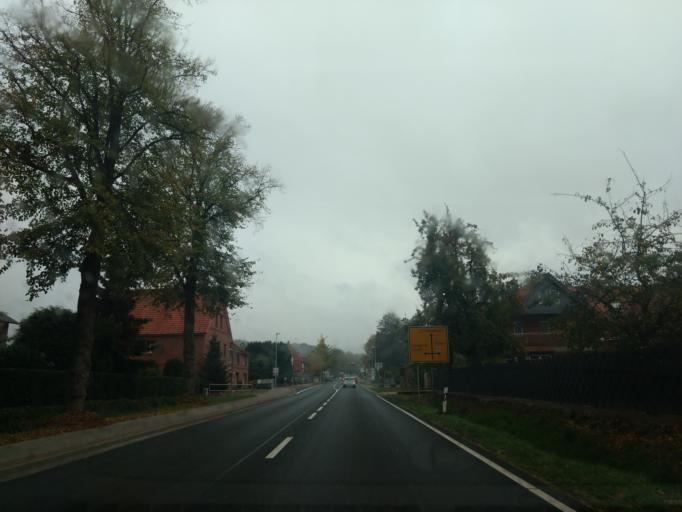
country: DE
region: Lower Saxony
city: Bad Iburg
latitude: 52.1477
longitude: 8.0365
